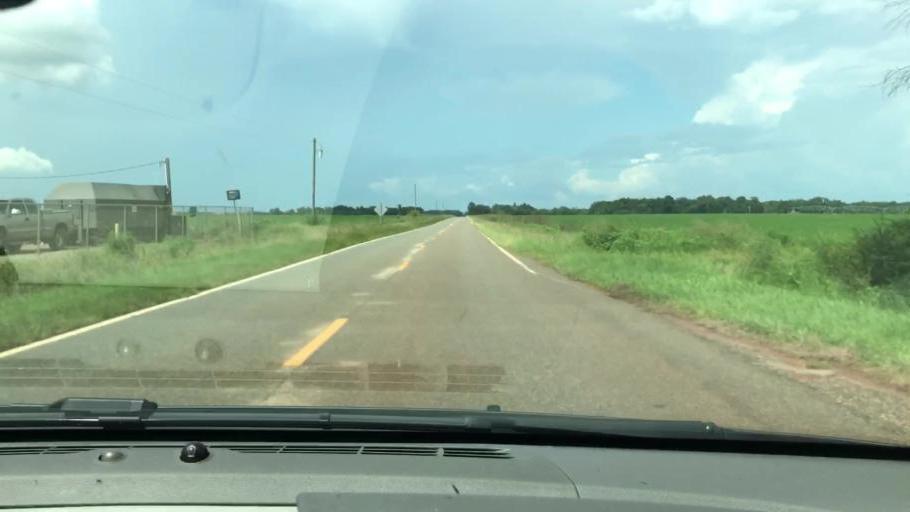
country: US
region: Georgia
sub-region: Seminole County
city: Donalsonville
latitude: 31.0983
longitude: -84.9961
